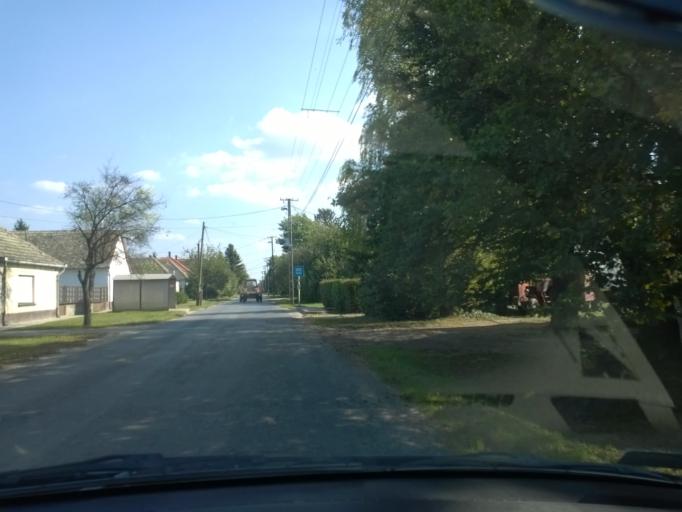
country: HU
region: Bacs-Kiskun
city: Hajos
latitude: 46.4836
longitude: 19.0808
